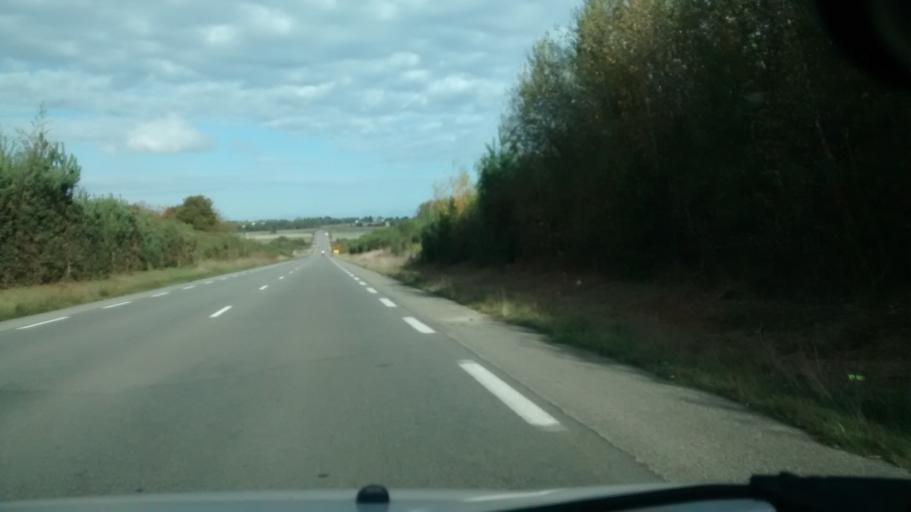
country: FR
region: Pays de la Loire
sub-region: Departement de Maine-et-Loire
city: Pouance
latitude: 47.7475
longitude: -1.2046
